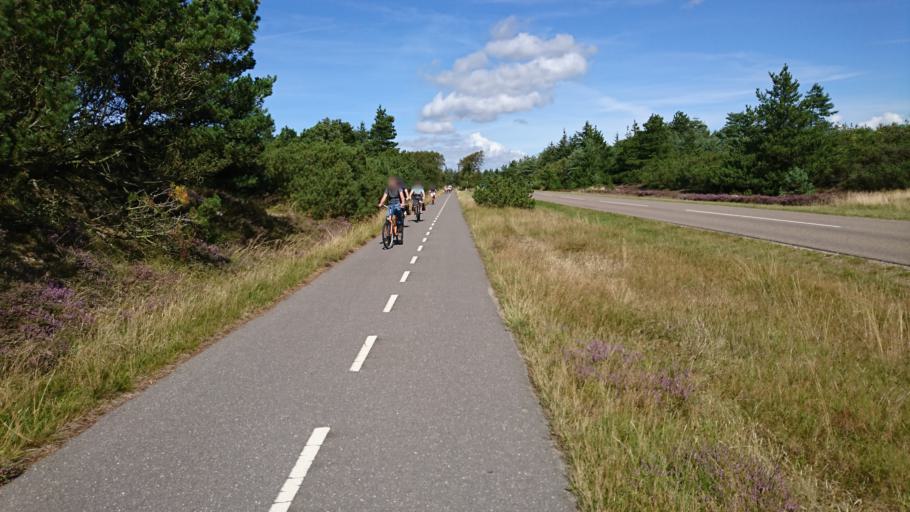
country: DK
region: South Denmark
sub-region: Fano Kommune
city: Nordby
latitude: 55.3919
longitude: 8.4245
